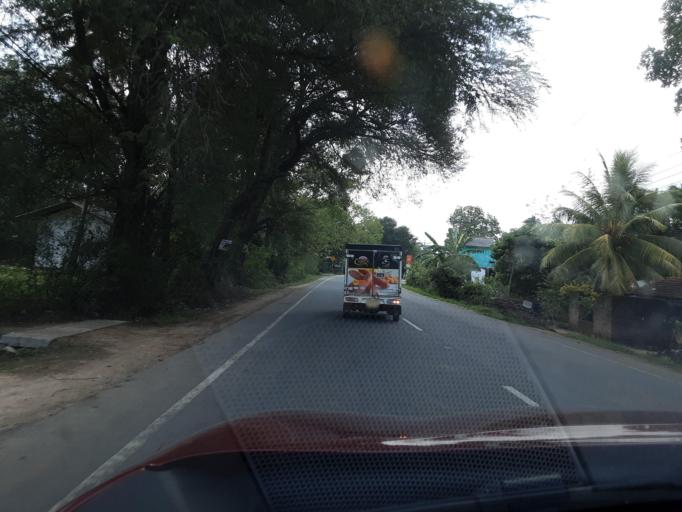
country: LK
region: Uva
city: Haputale
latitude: 6.6858
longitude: 81.1082
